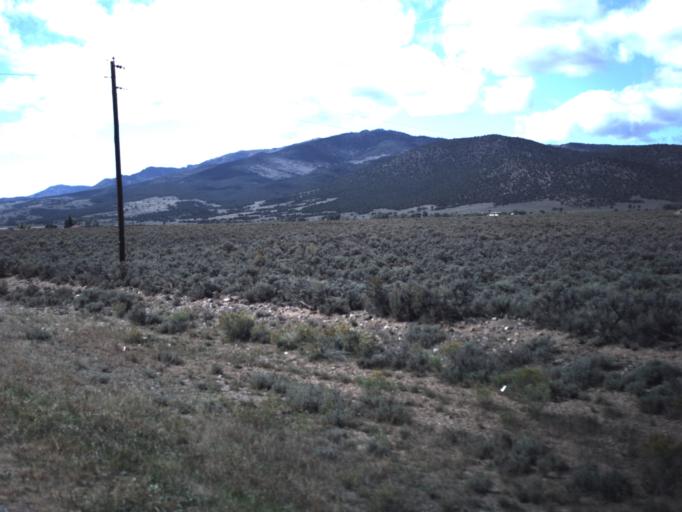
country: US
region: Utah
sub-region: Sevier County
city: Monroe
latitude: 38.4404
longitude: -111.9190
